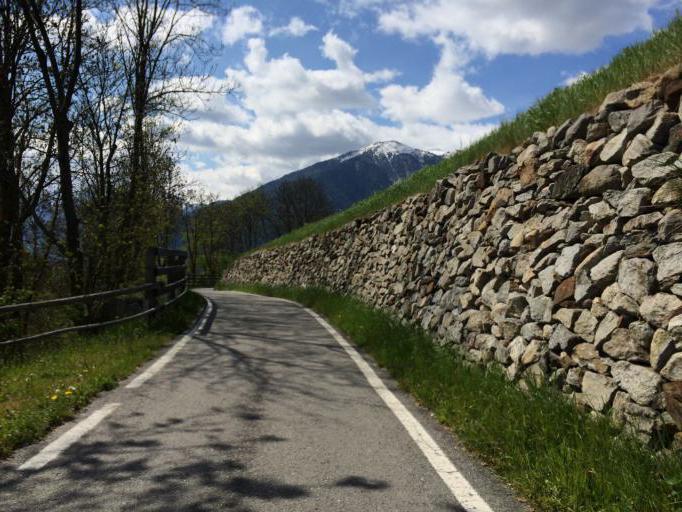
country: IT
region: Trentino-Alto Adige
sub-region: Bolzano
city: Malles Venosta
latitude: 46.7051
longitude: 10.5256
